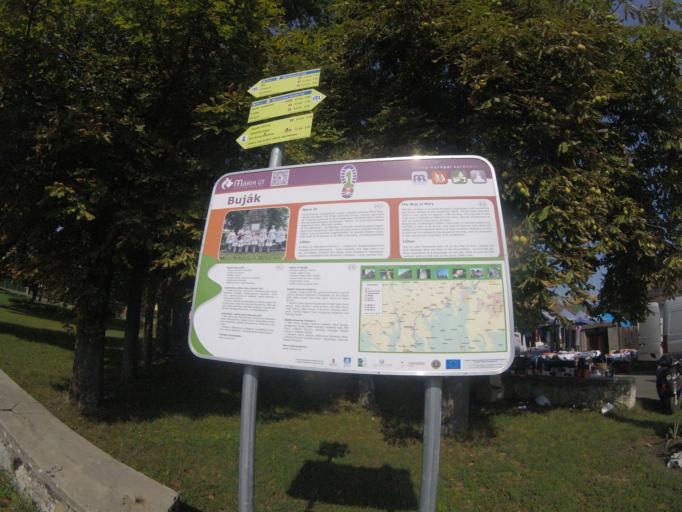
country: HU
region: Nograd
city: Bujak
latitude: 47.8820
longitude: 19.5420
